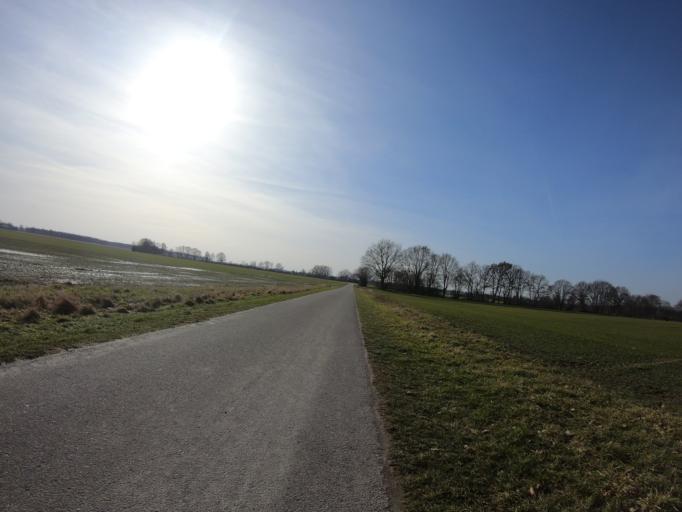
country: DE
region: Lower Saxony
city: Meine
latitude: 52.3952
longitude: 10.5594
